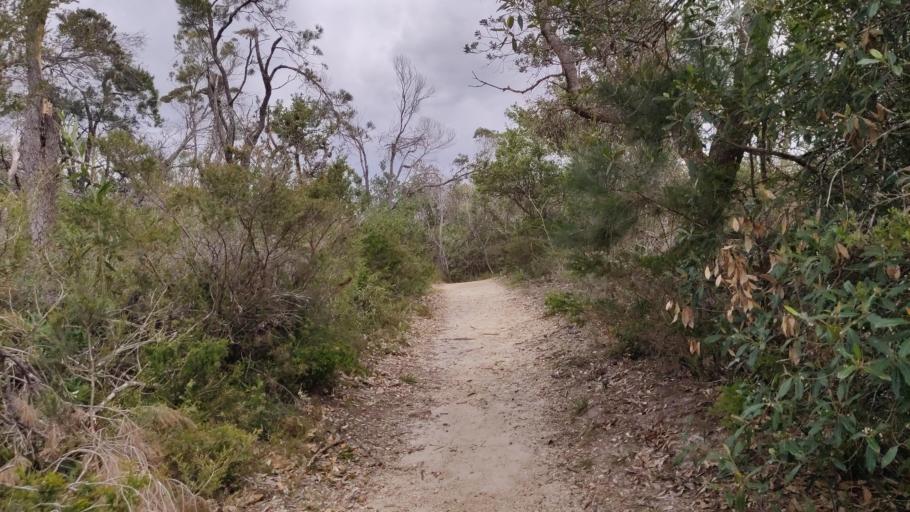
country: AU
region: New South Wales
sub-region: Port Macquarie-Hastings
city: North Haven
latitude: -31.6419
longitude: 152.8392
